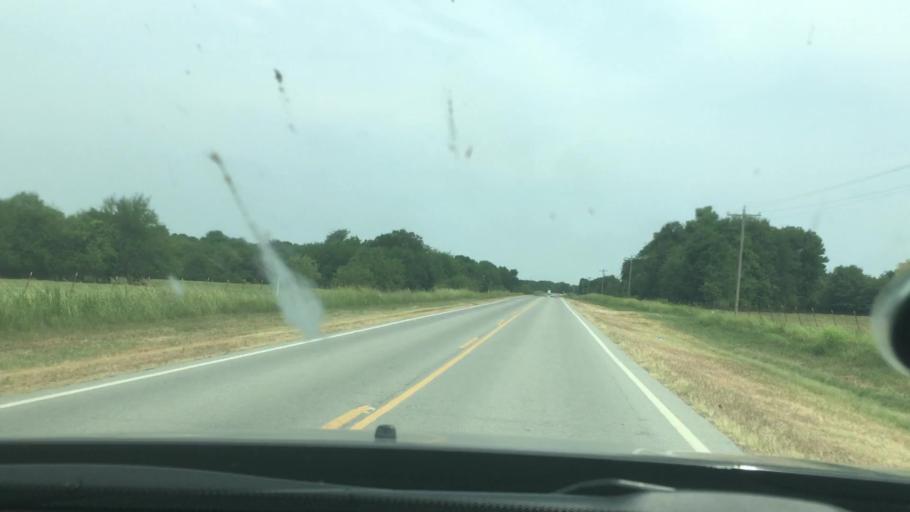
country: US
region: Oklahoma
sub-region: Coal County
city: Coalgate
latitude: 34.5862
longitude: -96.4163
